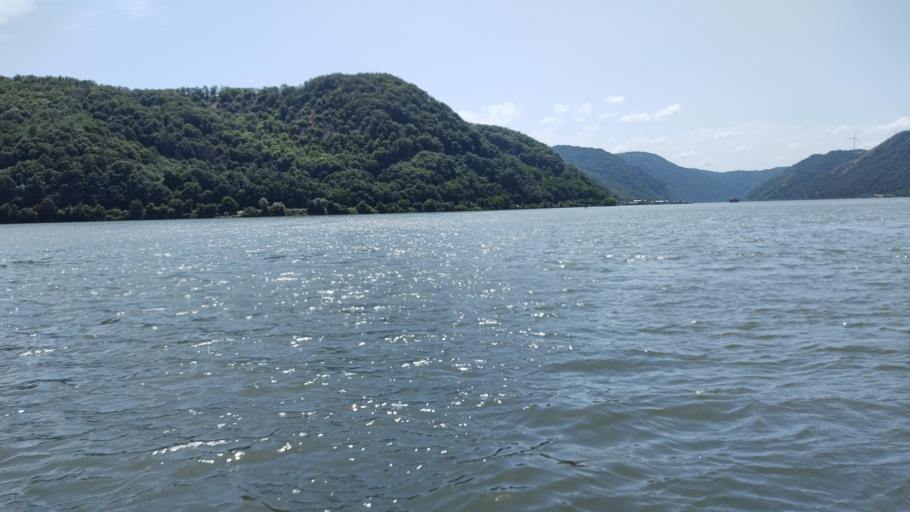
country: RS
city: Radenka
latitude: 44.6602
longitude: 21.7817
